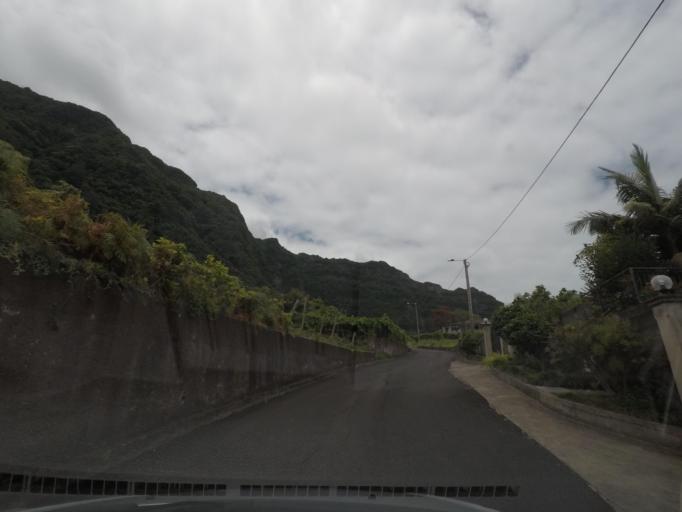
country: PT
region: Madeira
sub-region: Santana
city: Santana
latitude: 32.8268
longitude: -16.9500
